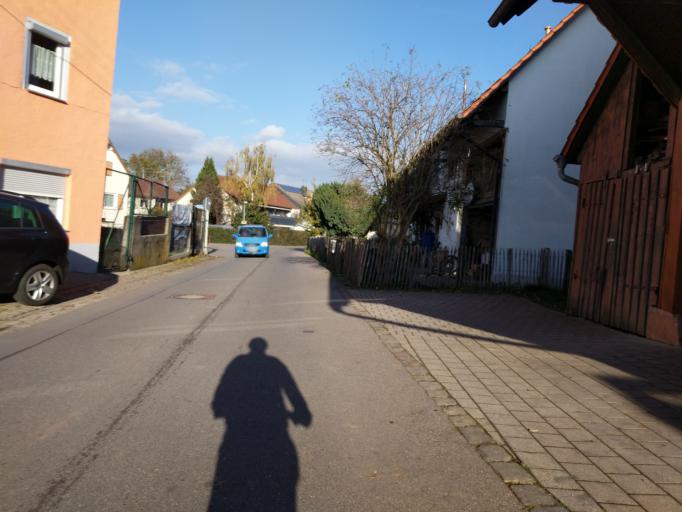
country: DE
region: Baden-Wuerttemberg
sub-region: Tuebingen Region
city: Tuebingen
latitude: 48.4884
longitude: 9.0188
